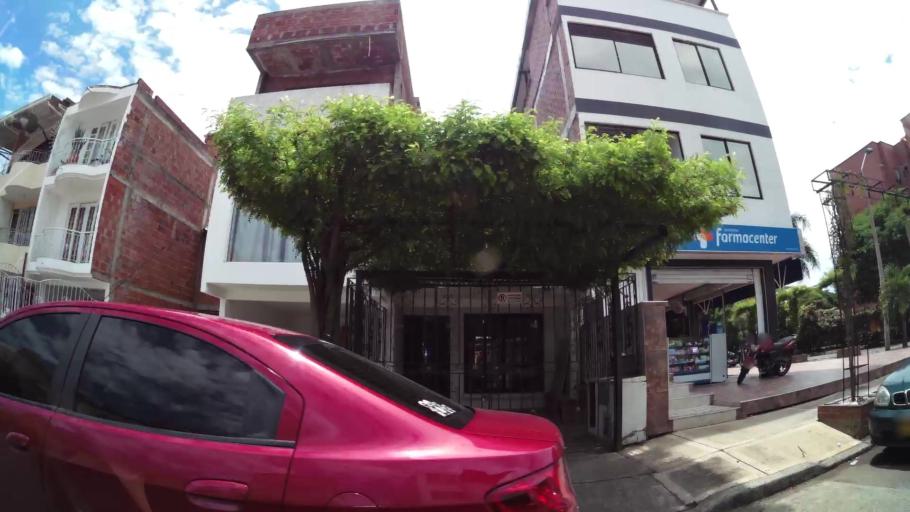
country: CO
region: Valle del Cauca
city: Cali
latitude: 3.3731
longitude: -76.5187
